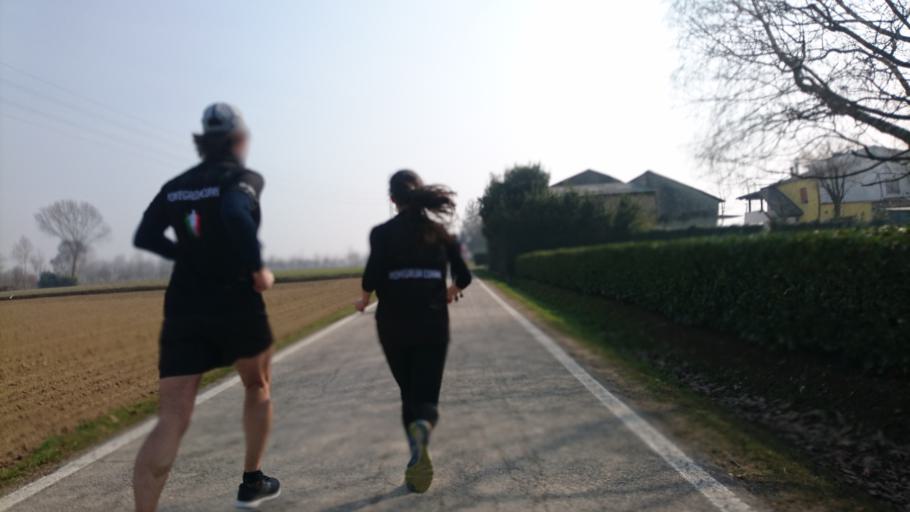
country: IT
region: Veneto
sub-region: Provincia di Vicenza
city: Montegalda
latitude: 45.4748
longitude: 11.6690
